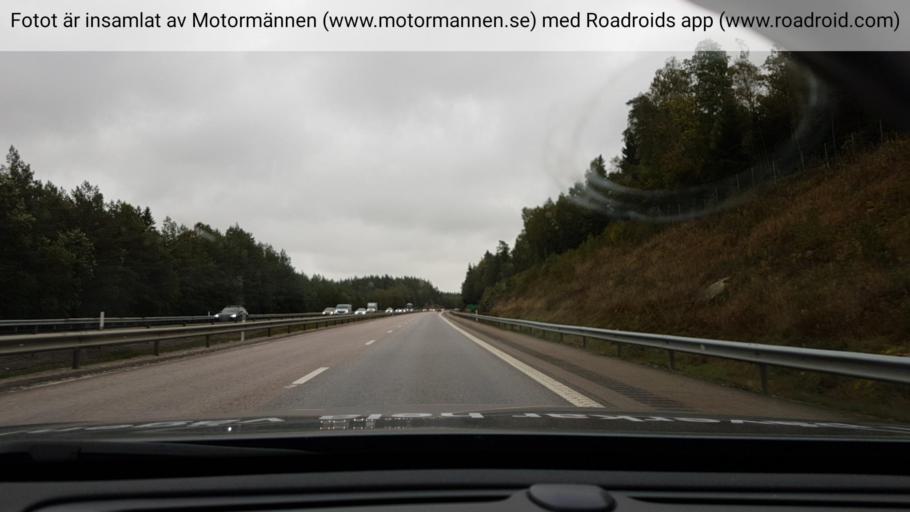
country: SE
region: Vaestra Goetaland
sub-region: Harryda Kommun
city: Landvetter
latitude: 57.6854
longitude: 12.2861
